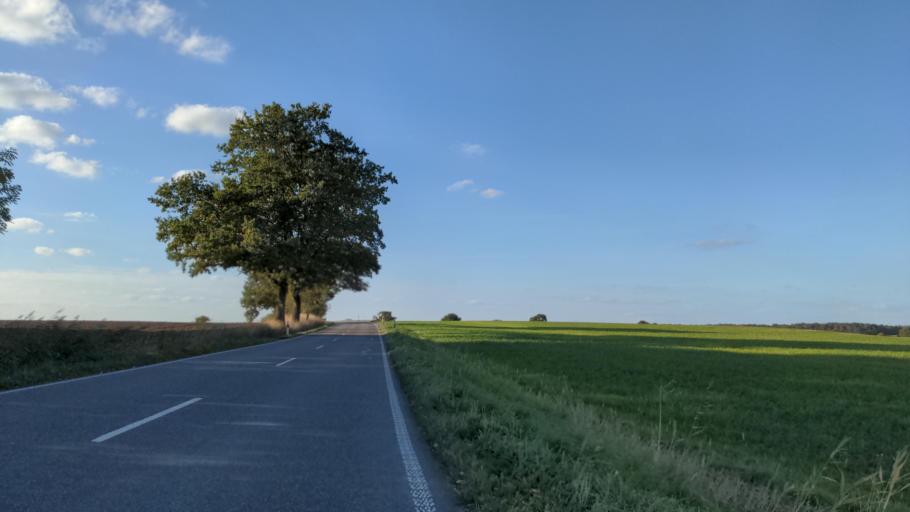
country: DE
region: Schleswig-Holstein
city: Pronstorf
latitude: 53.9615
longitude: 10.5158
